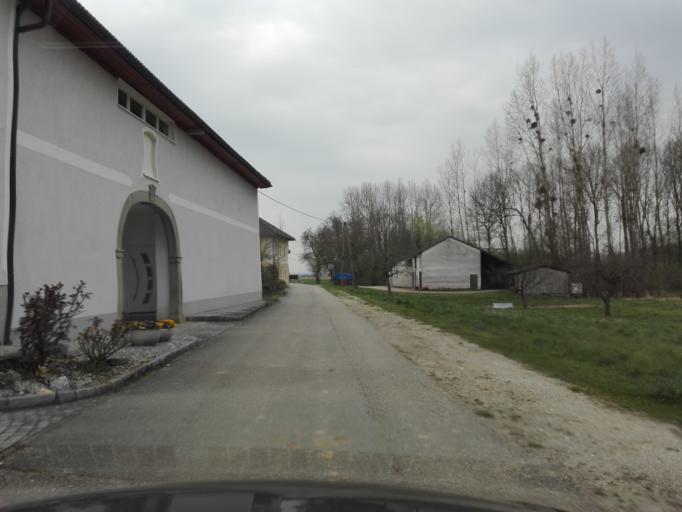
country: AT
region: Upper Austria
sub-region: Politischer Bezirk Perg
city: Perg
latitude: 48.2429
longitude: 14.5961
